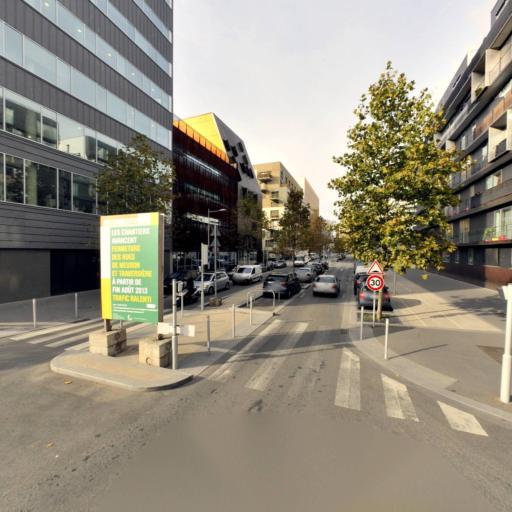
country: FR
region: Ile-de-France
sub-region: Departement des Hauts-de-Seine
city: Boulogne-Billancourt
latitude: 48.8286
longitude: 2.2387
